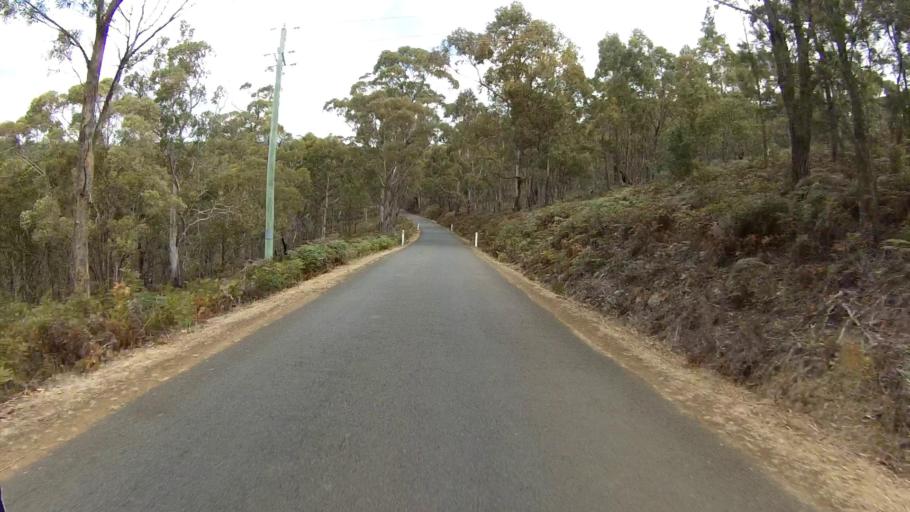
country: AU
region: Tasmania
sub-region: Sorell
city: Sorell
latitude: -42.6014
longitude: 147.9248
